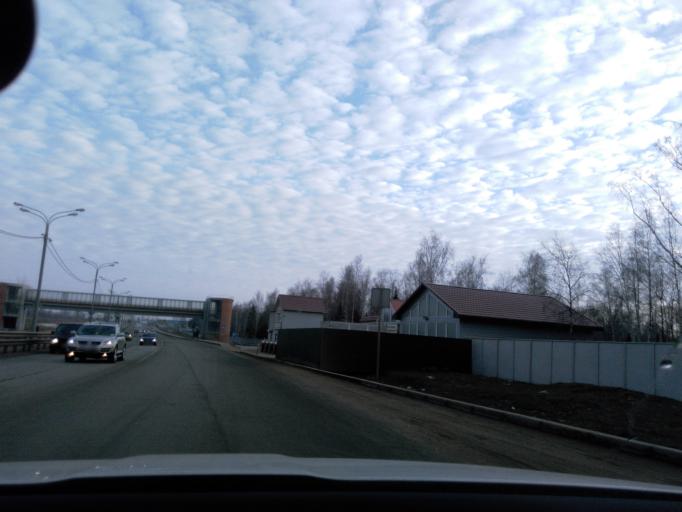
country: RU
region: Moscow
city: Businovo
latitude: 55.9064
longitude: 37.4933
